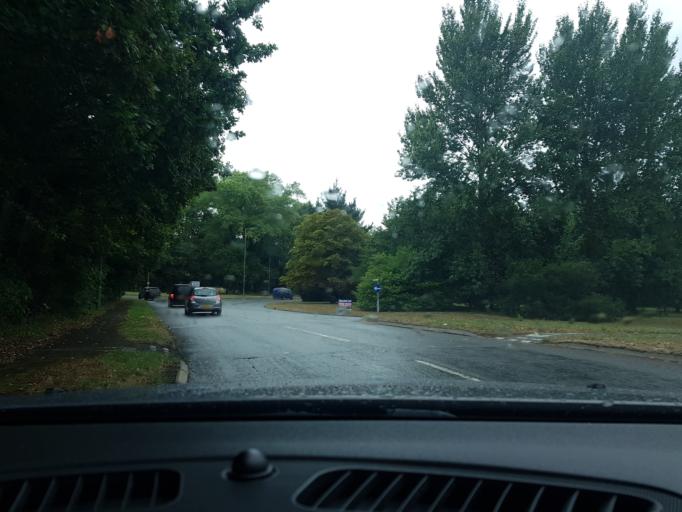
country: GB
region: England
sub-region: Surrey
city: Hale
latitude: 51.2246
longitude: -0.7823
